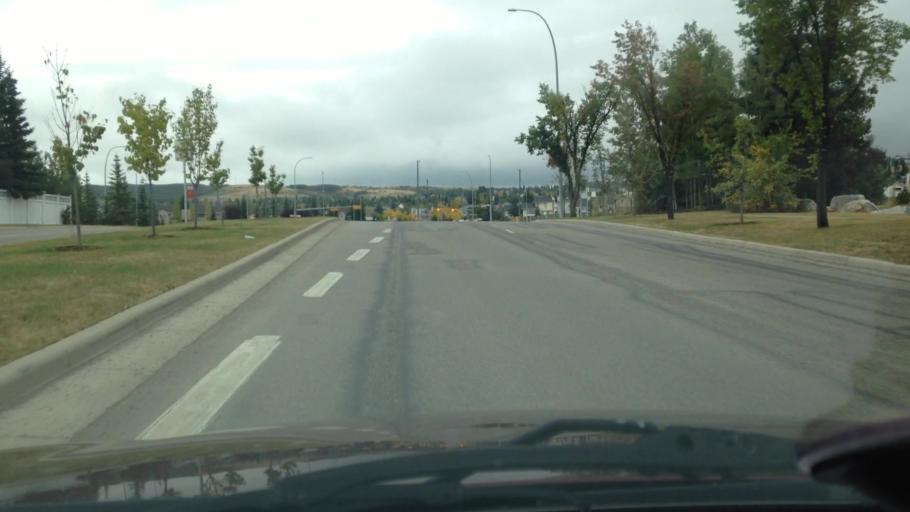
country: CA
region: Alberta
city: Calgary
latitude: 51.1450
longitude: -114.1071
